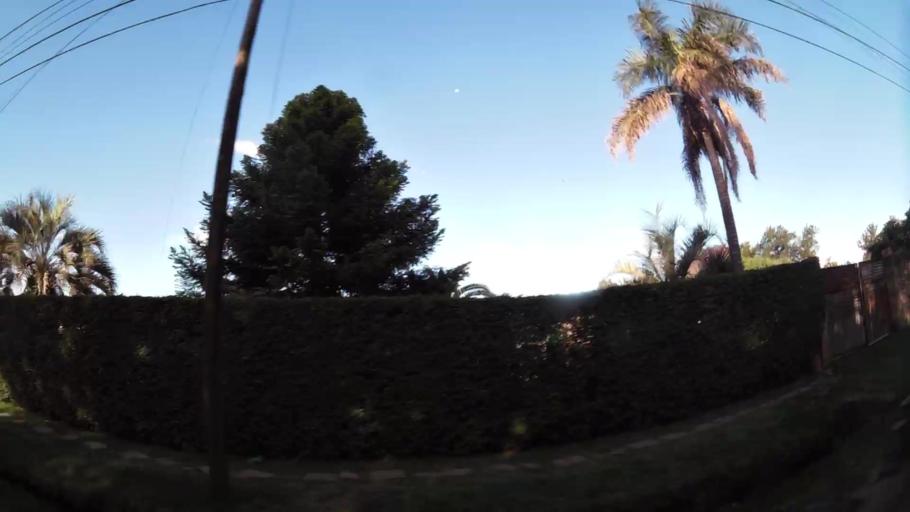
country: AR
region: Buenos Aires
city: Santa Catalina - Dique Lujan
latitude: -34.4714
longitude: -58.7493
